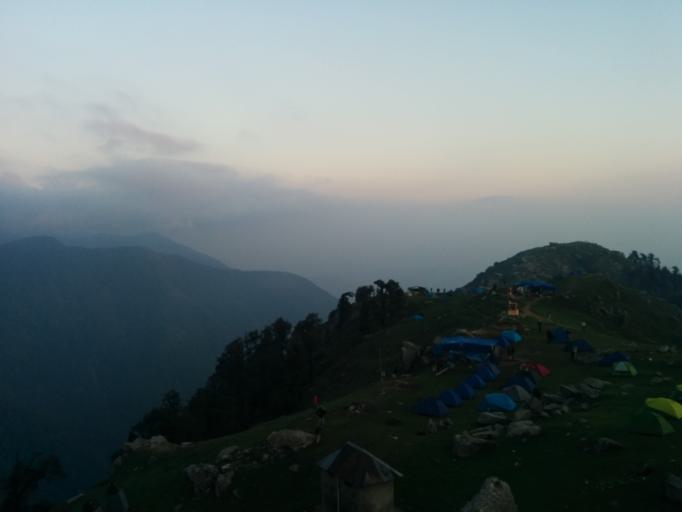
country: IN
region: Himachal Pradesh
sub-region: Kangra
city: Dharmsala
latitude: 32.2620
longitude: 76.3545
